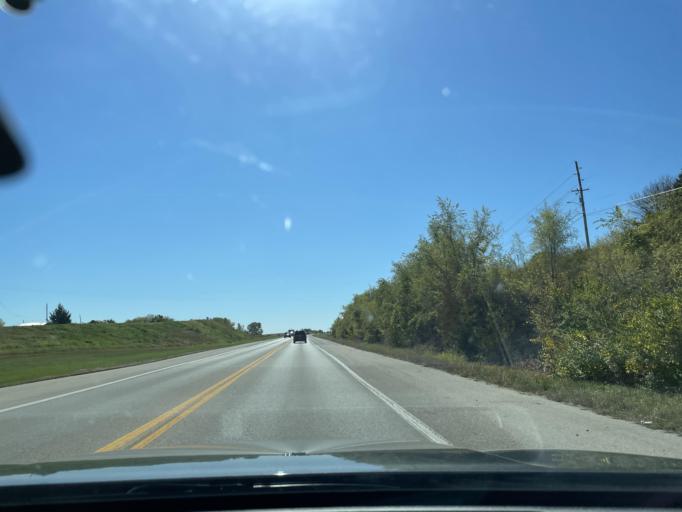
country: US
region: Missouri
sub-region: Andrew County
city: Country Club Village
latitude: 39.7805
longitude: -94.7675
